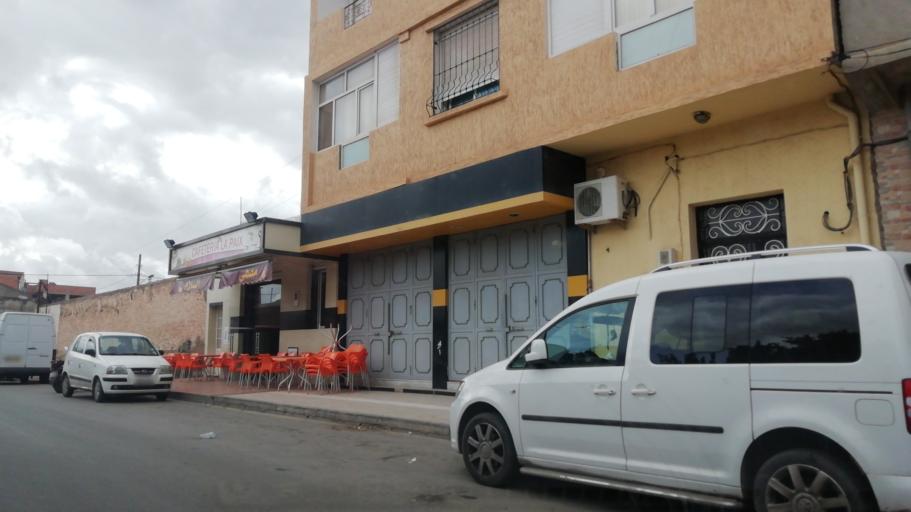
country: DZ
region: Oran
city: Oran
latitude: 35.6880
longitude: -0.6522
